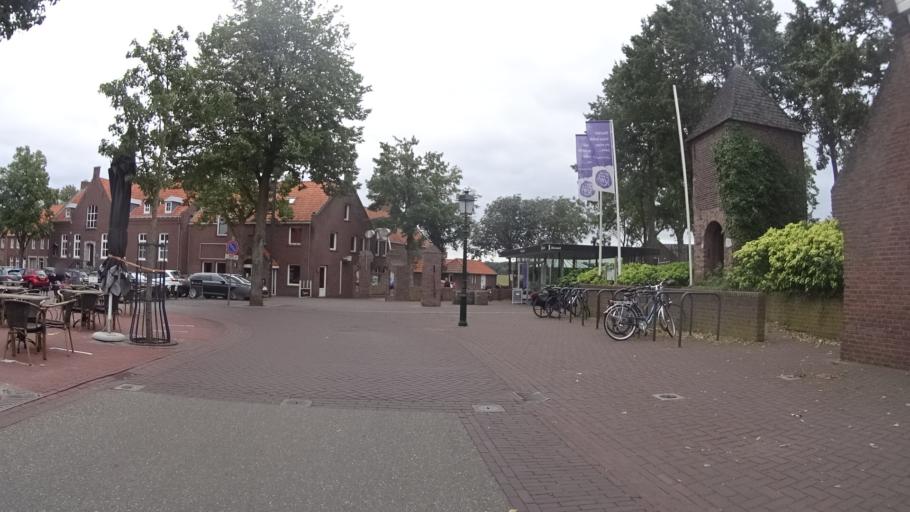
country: NL
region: Limburg
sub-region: Gemeente Beesel
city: Reuver
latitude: 51.2914
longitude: 6.0567
